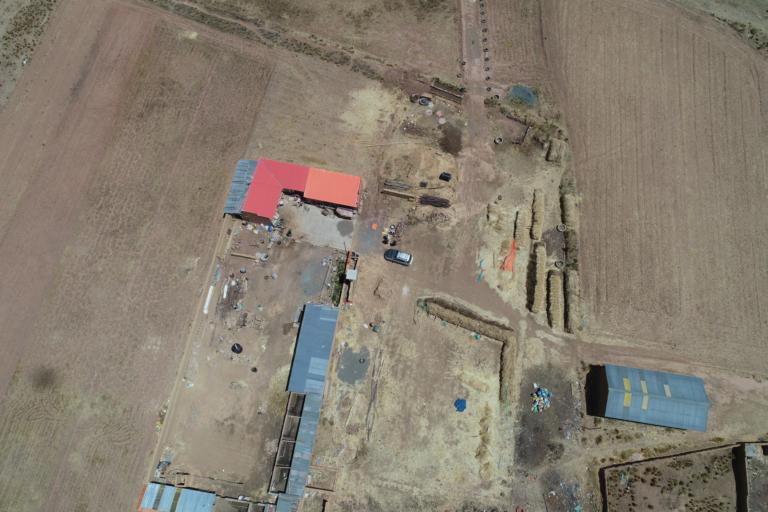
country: BO
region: La Paz
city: Achacachi
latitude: -15.9116
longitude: -68.8873
